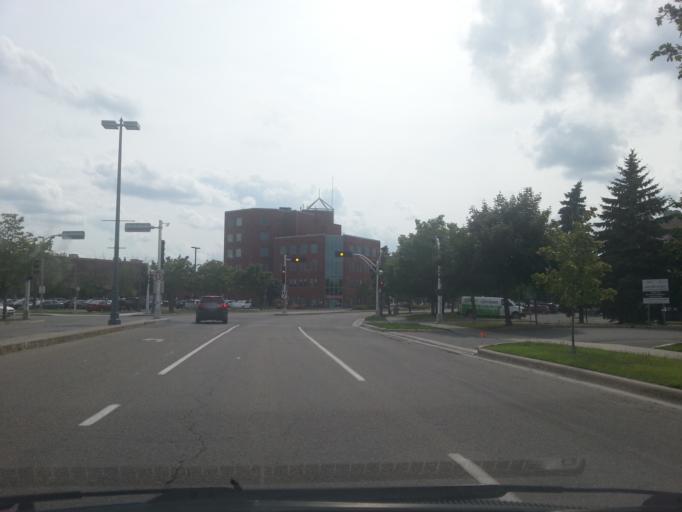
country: CA
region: Quebec
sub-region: Outaouais
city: Gatineau
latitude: 45.4828
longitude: -75.6858
